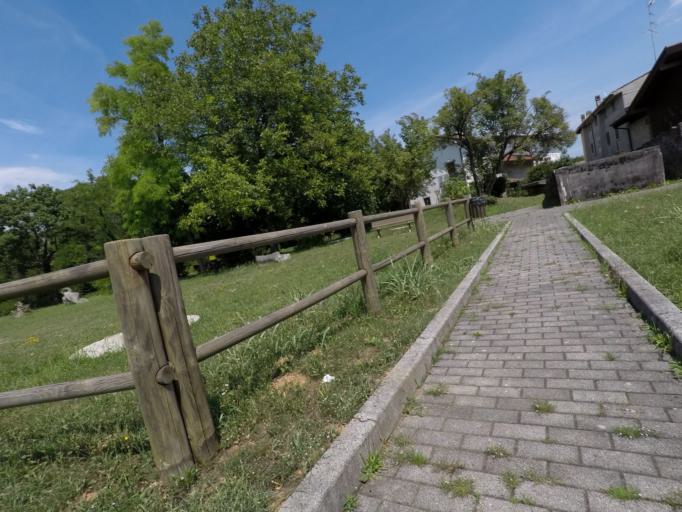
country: IT
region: Friuli Venezia Giulia
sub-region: Provincia di Pordenone
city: Lestans
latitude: 46.1646
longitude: 12.8968
